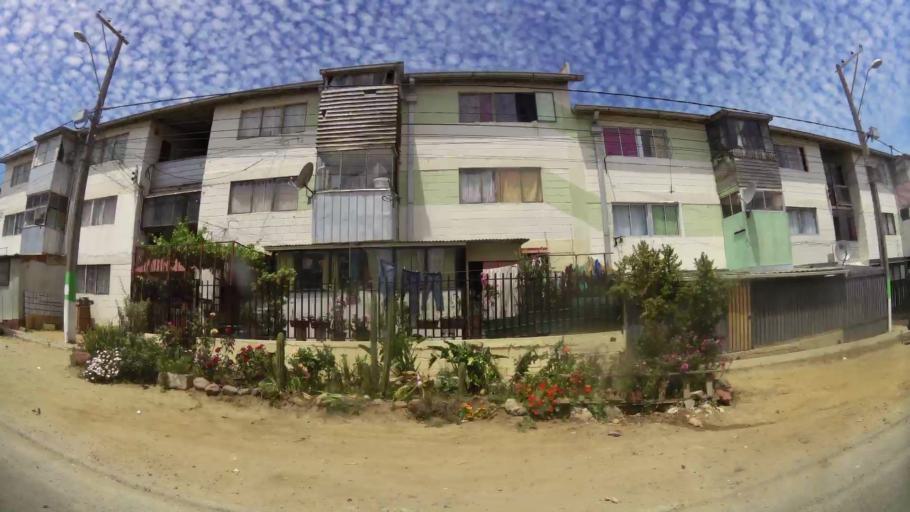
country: CL
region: Valparaiso
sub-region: Provincia de Valparaiso
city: Vina del Mar
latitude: -33.0588
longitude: -71.5617
